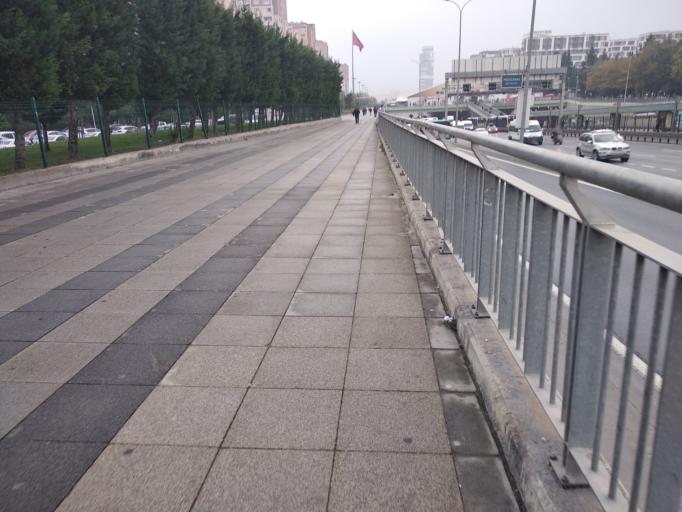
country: TR
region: Istanbul
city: Esenyurt
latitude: 41.0130
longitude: 28.6487
